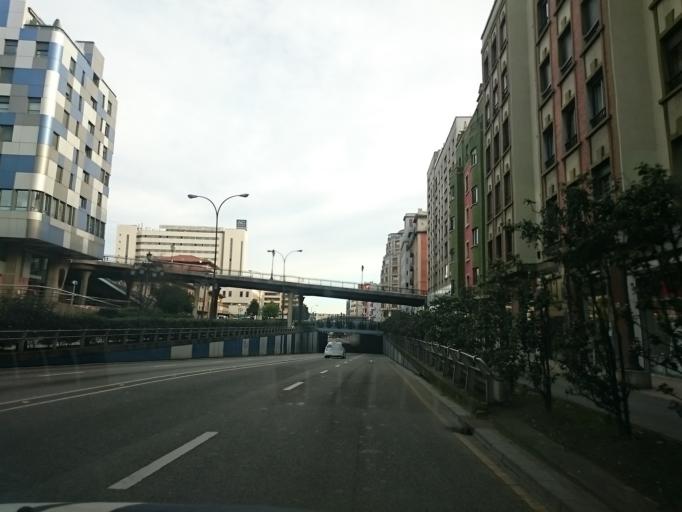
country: ES
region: Asturias
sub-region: Province of Asturias
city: Oviedo
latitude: 43.3652
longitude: -5.8401
